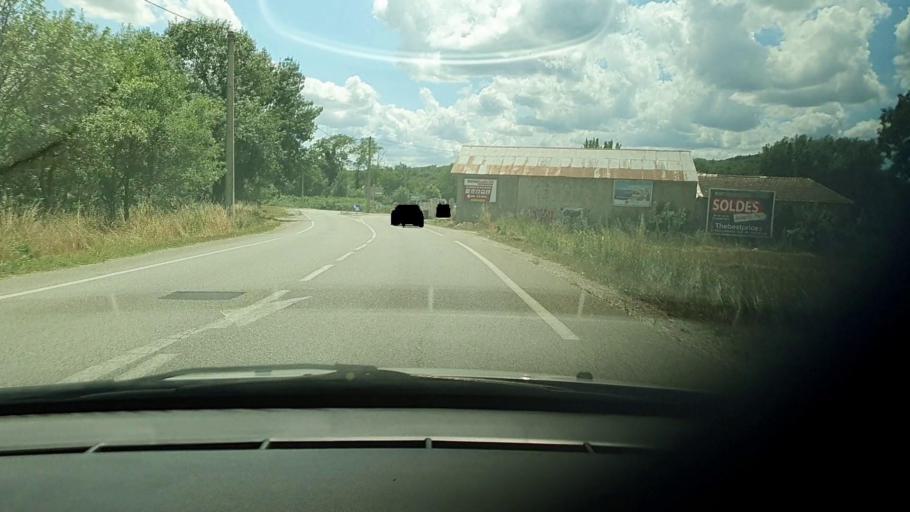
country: FR
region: Languedoc-Roussillon
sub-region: Departement du Gard
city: Moussac
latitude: 43.9786
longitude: 4.2093
